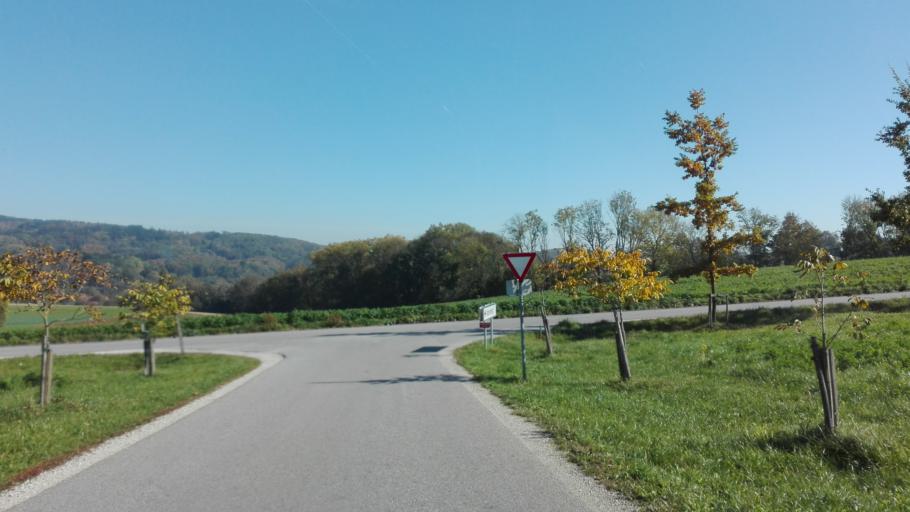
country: AT
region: Upper Austria
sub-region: Politischer Bezirk Linz-Land
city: Pasching
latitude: 48.2848
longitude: 14.1845
